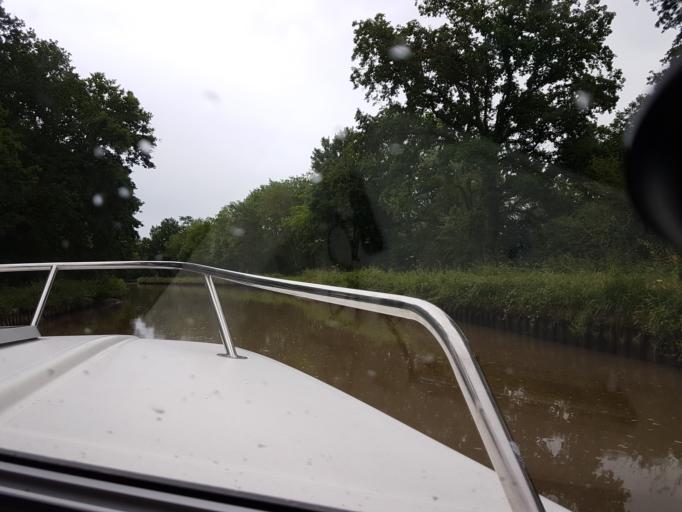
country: FR
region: Bourgogne
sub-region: Departement de la Nievre
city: Clamecy
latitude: 47.3726
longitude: 3.6066
